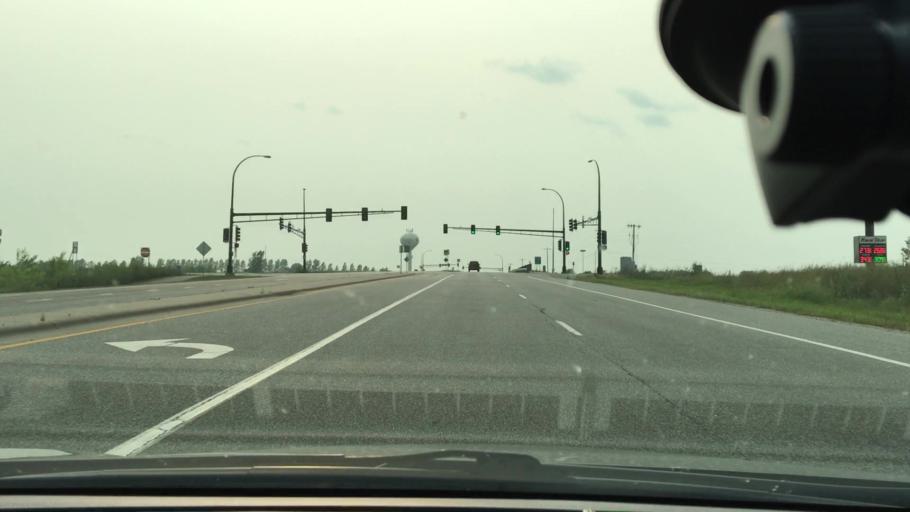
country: US
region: Minnesota
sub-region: Hennepin County
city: Dayton
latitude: 45.2525
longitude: -93.5521
